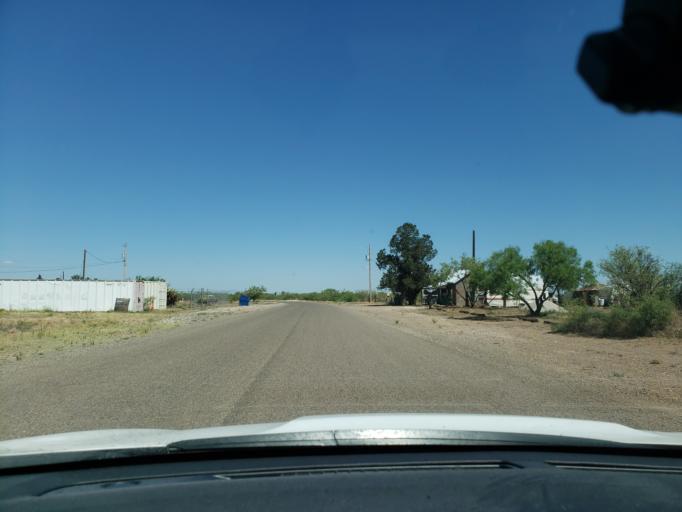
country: US
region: Texas
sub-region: Presidio County
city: Marfa
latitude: 30.5886
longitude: -104.4959
